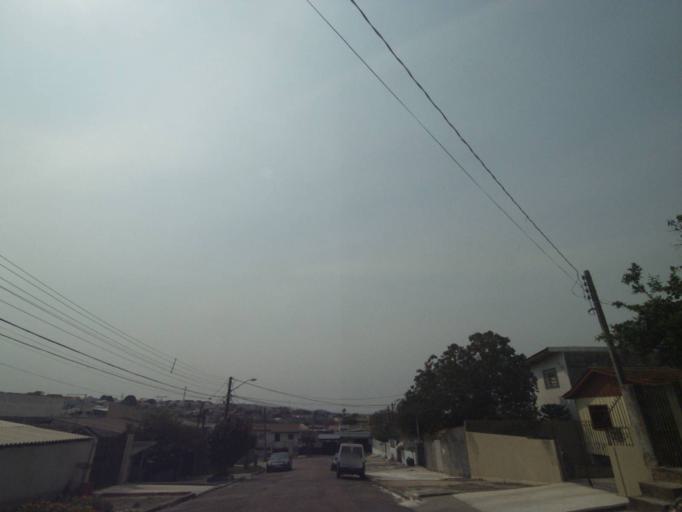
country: BR
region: Parana
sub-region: Sao Jose Dos Pinhais
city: Sao Jose dos Pinhais
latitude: -25.5210
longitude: -49.2859
